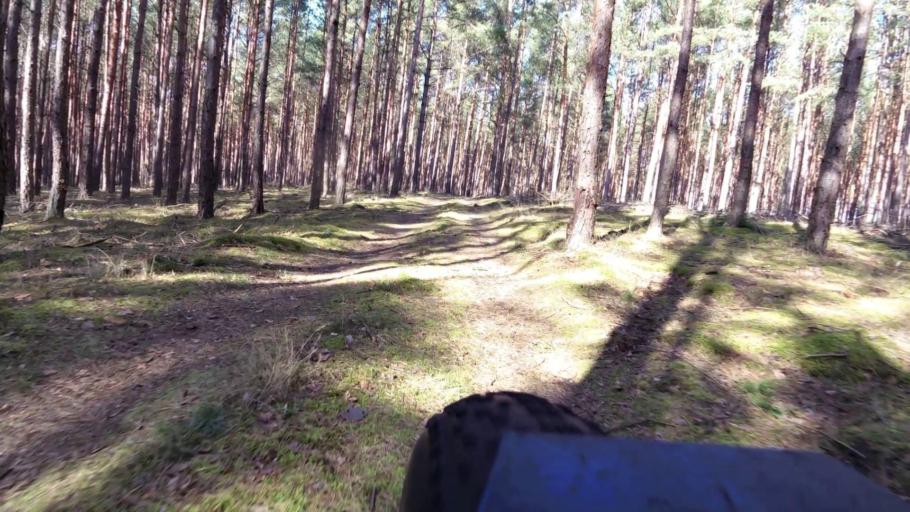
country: PL
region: Lubusz
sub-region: Powiat slubicki
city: Cybinka
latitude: 52.2090
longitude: 14.9282
